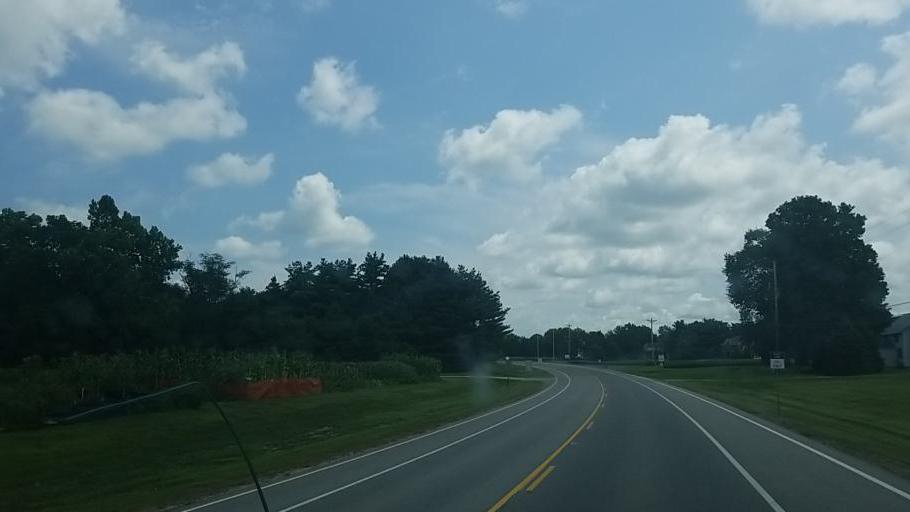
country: US
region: Ohio
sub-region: Fairfield County
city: Pickerington
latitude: 39.8787
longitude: -82.7321
